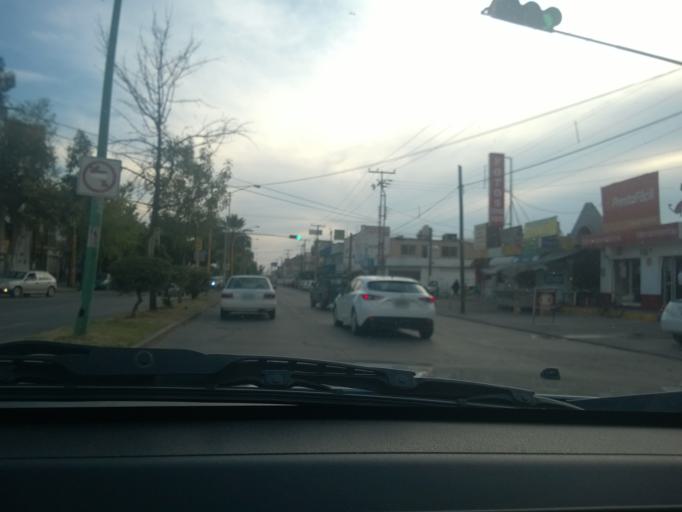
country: MX
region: Guanajuato
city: Leon
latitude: 21.1364
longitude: -101.6632
